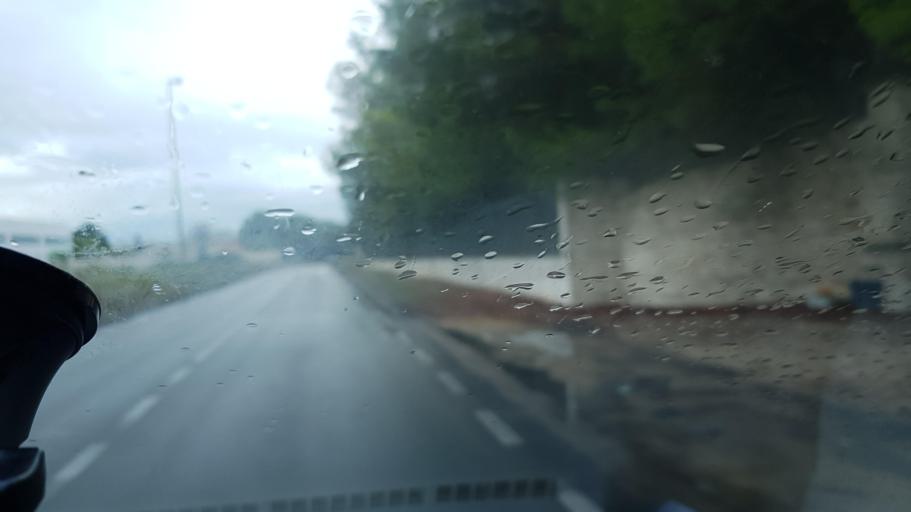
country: IT
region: Apulia
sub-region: Provincia di Lecce
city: Giorgilorio
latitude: 40.3762
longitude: 18.1371
